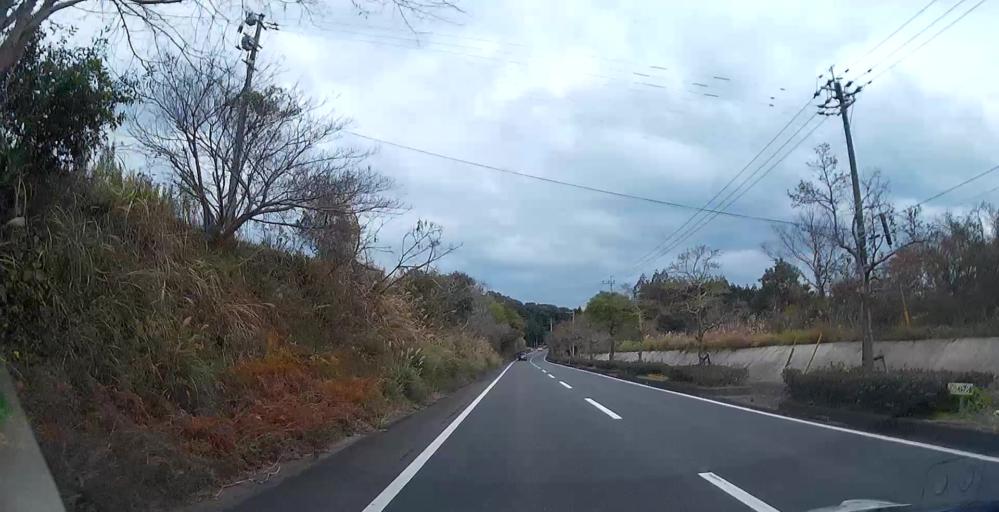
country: JP
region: Kagoshima
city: Akune
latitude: 32.0719
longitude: 130.2159
